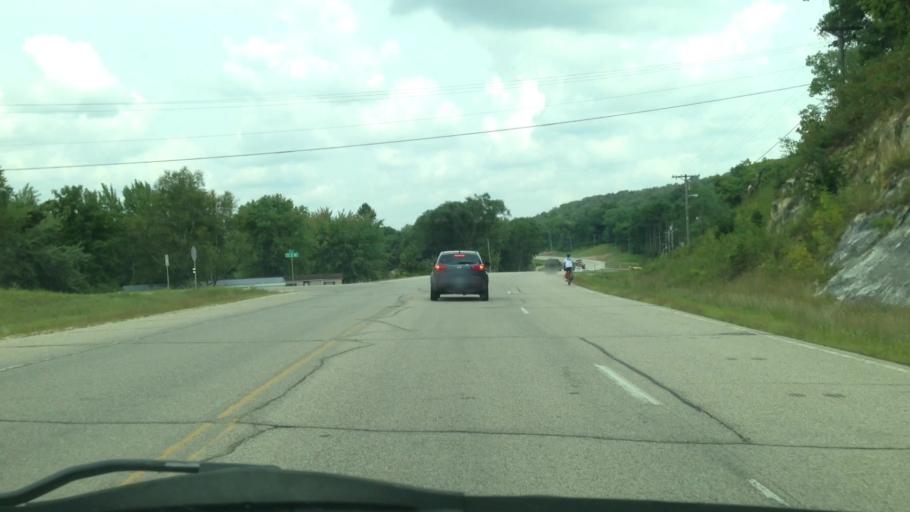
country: US
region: Minnesota
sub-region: Olmsted County
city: Rochester
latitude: 44.0787
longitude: -92.4500
